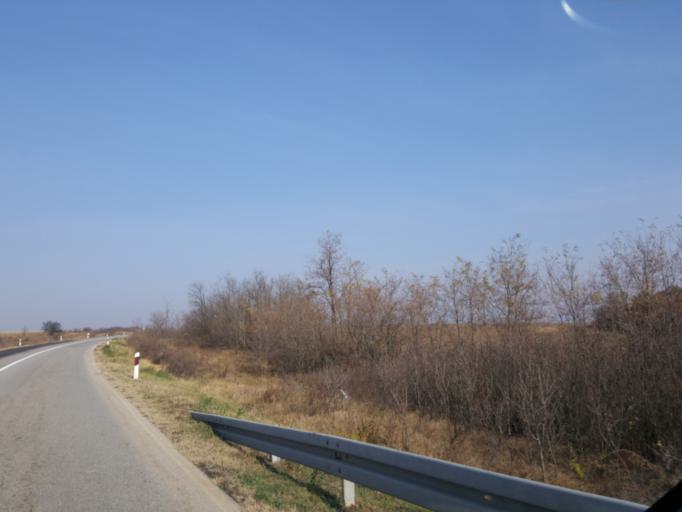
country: RS
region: Central Serbia
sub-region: Zajecarski Okrug
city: Zajecar
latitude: 44.0602
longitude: 22.3331
